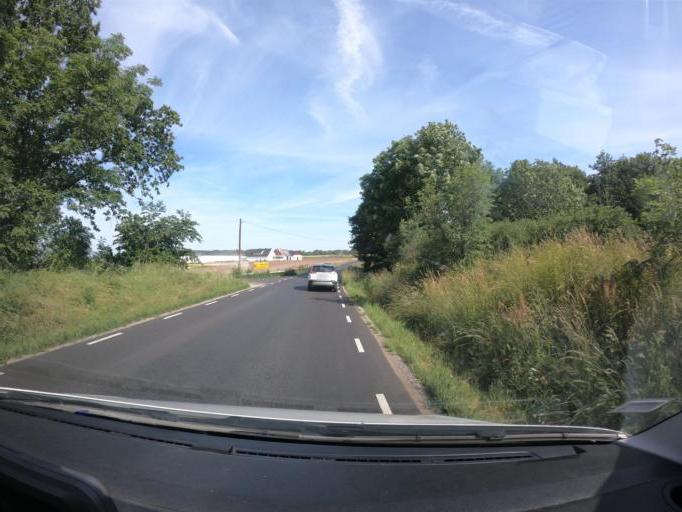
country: SE
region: Skane
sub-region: Angelholms Kommun
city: Vejbystrand
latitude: 56.3935
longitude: 12.7023
